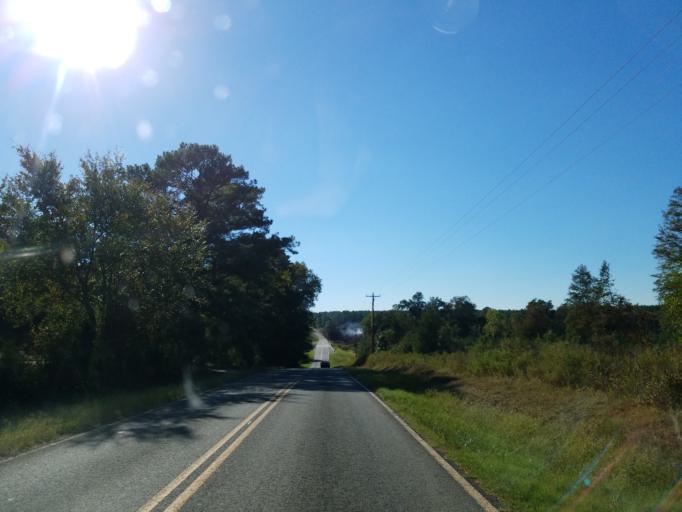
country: US
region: Georgia
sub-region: Dooly County
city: Unadilla
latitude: 32.2447
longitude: -83.8334
